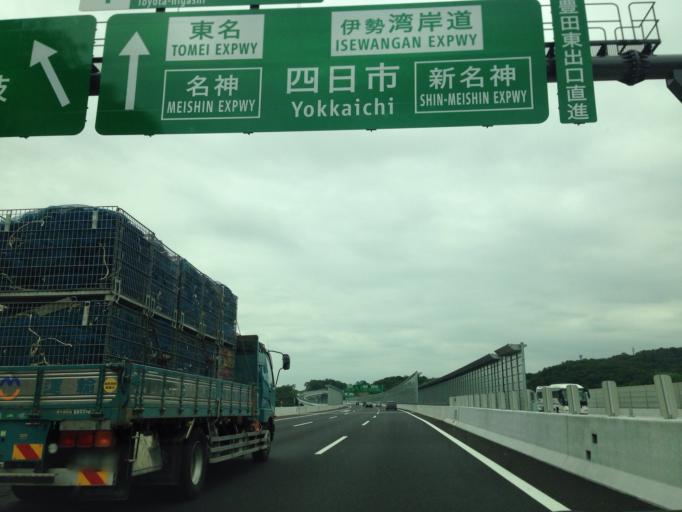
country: JP
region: Aichi
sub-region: Toyota-shi
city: Toyota
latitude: 35.0424
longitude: 137.2048
